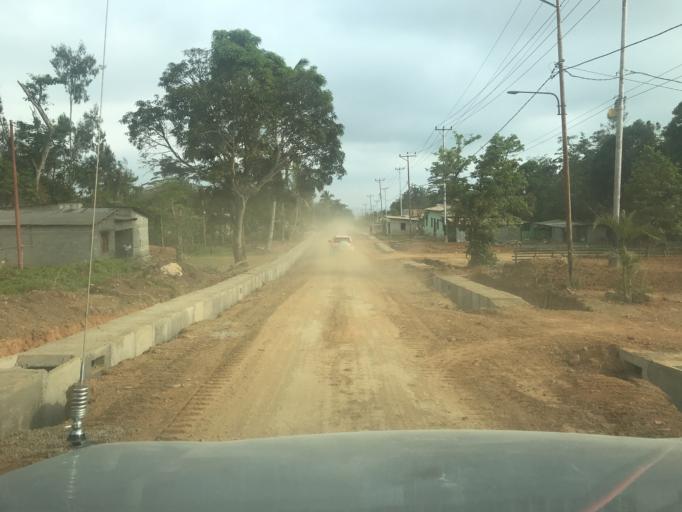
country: TL
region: Ainaro
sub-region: Ainaro
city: Ainaro
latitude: -9.0020
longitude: 125.5007
